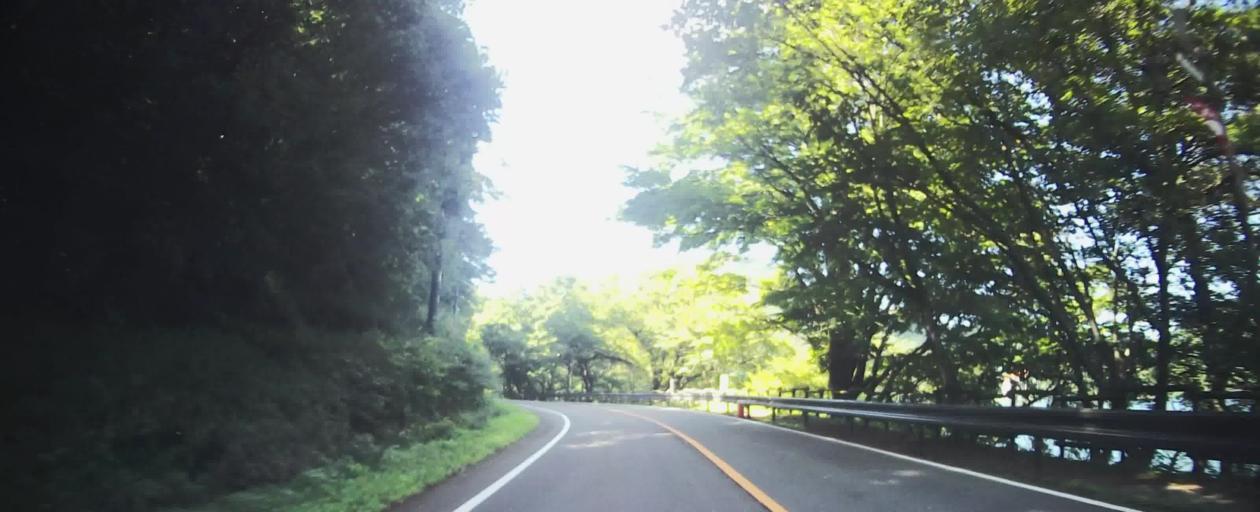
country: JP
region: Gunma
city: Nakanojomachi
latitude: 36.4684
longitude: 138.8684
